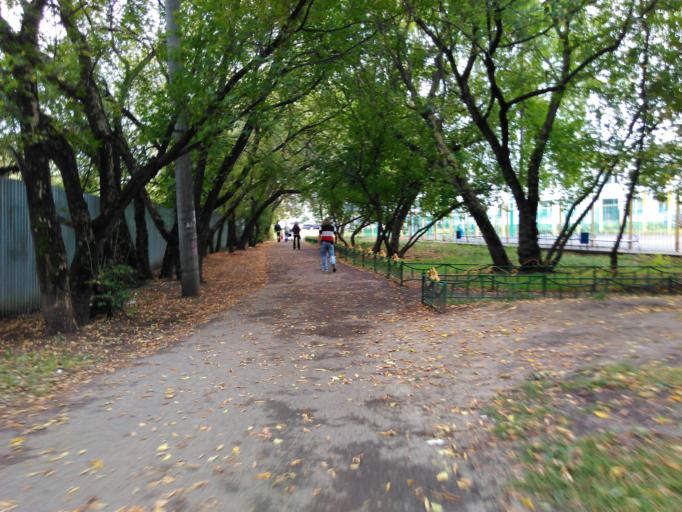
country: RU
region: Moscow
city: Leonovo
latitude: 55.8402
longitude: 37.6436
